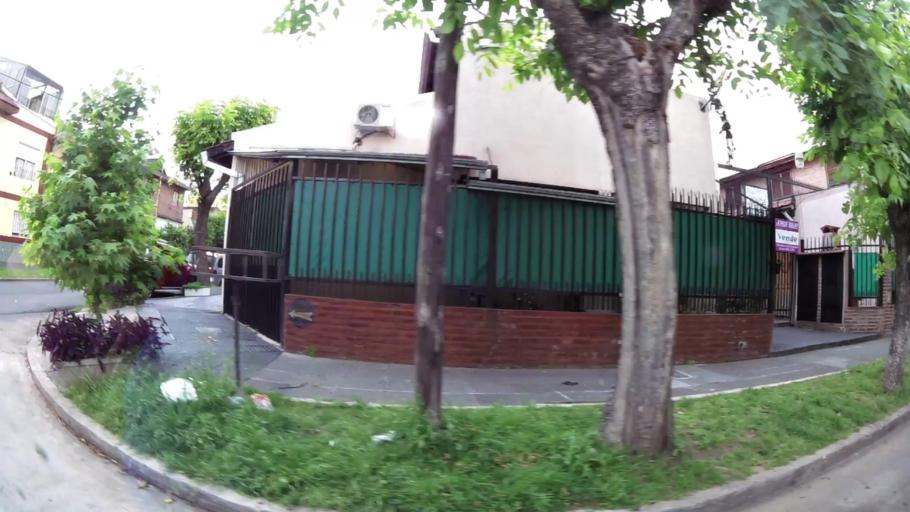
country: AR
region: Buenos Aires
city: San Justo
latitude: -34.6613
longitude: -58.5220
